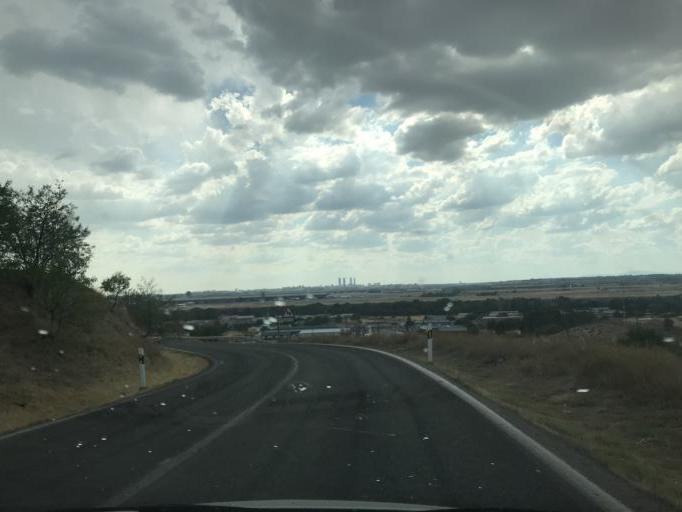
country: ES
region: Madrid
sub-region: Provincia de Madrid
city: Paracuellos de Jarama
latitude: 40.5050
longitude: -3.5388
